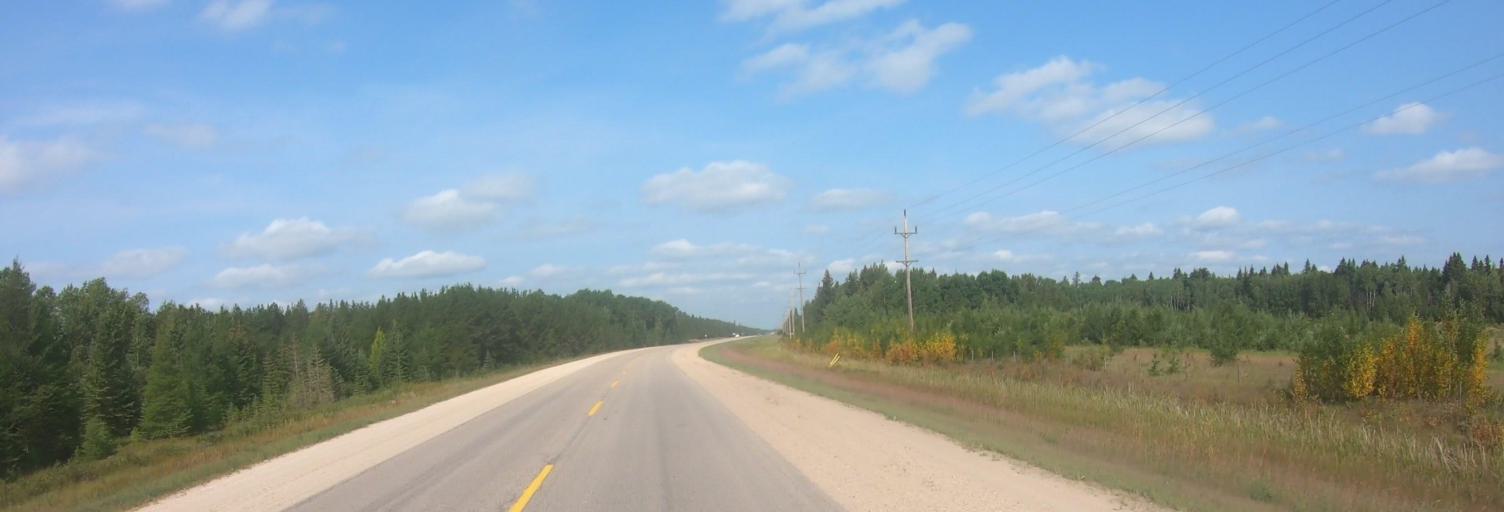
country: CA
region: Manitoba
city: La Broquerie
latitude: 49.1865
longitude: -96.2488
